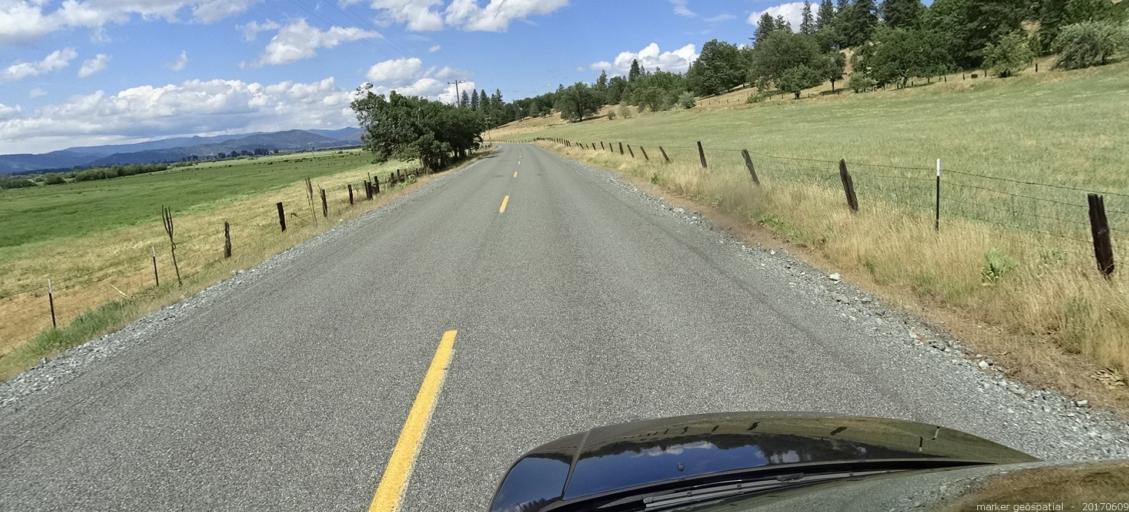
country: US
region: California
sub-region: Siskiyou County
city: Yreka
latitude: 41.4731
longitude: -122.8798
